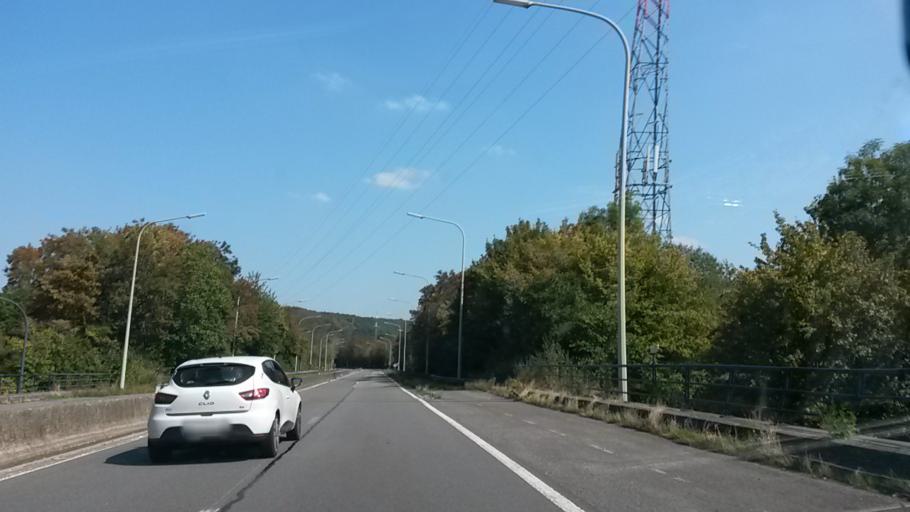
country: BE
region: Wallonia
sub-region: Province du Hainaut
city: Aiseau
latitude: 50.4501
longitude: 4.6047
